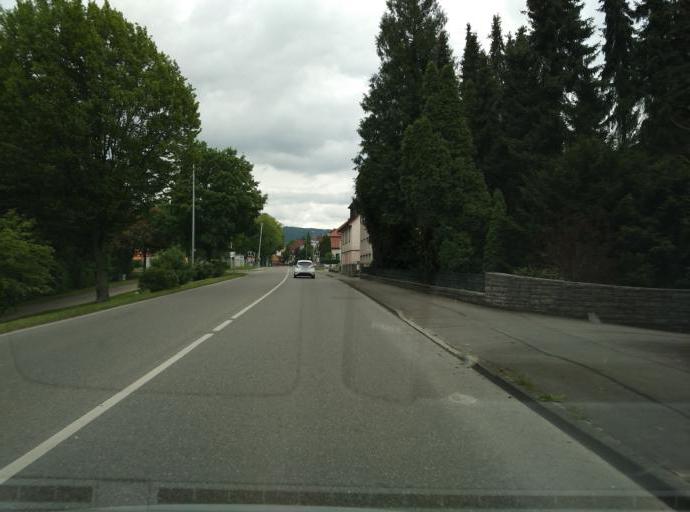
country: DE
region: Baden-Wuerttemberg
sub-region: Regierungsbezirk Stuttgart
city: Frickenhausen
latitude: 48.5963
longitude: 9.3560
